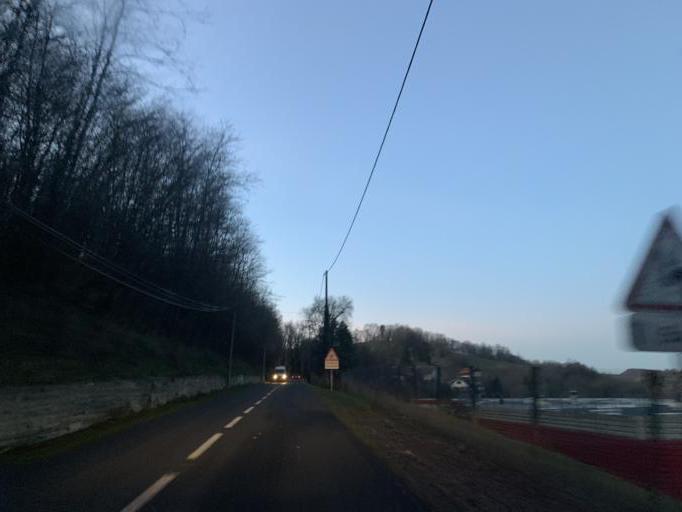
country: FR
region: Rhone-Alpes
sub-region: Departement de l'Ain
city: Belley
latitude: 45.7741
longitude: 5.6871
